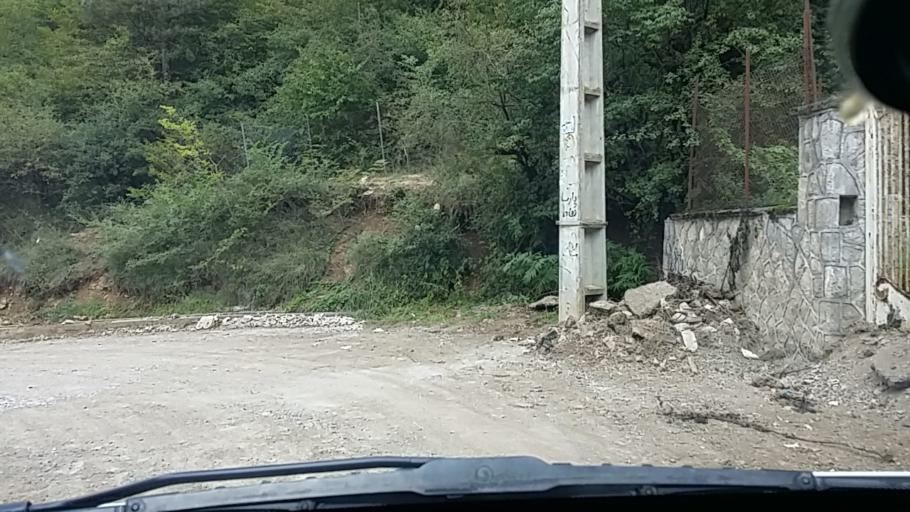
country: IR
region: Mazandaran
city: `Abbasabad
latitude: 36.4905
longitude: 51.1675
